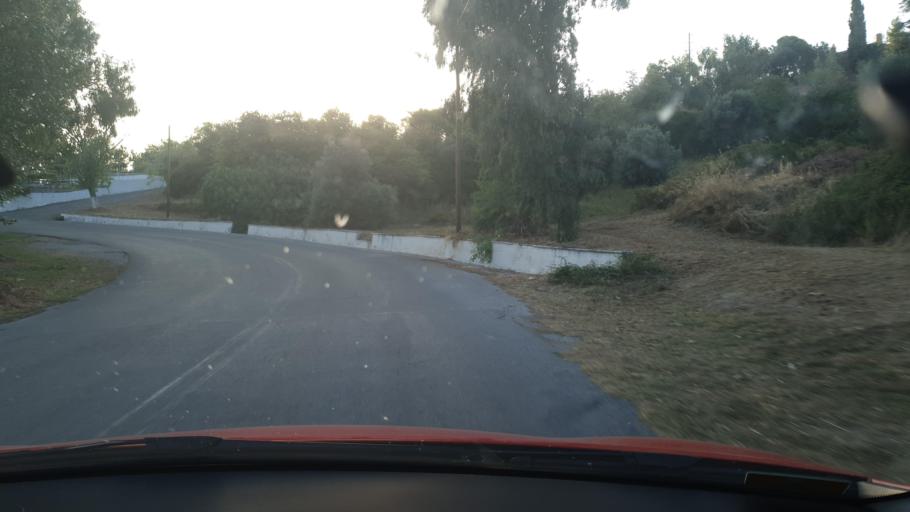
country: GR
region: Central Greece
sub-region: Nomos Evvoias
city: Oxilithos
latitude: 38.5740
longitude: 24.1170
